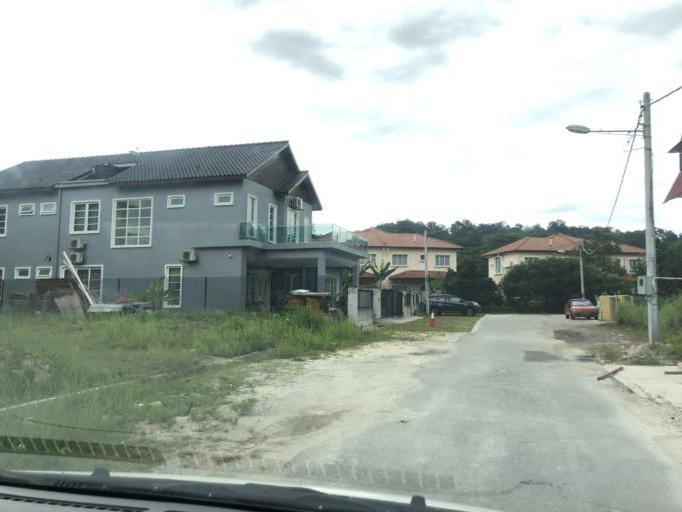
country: MY
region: Putrajaya
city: Putrajaya
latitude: 2.9223
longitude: 101.7600
